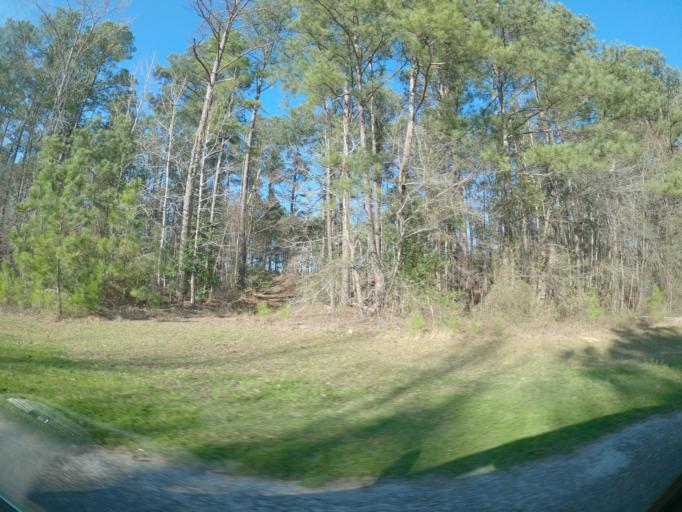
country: US
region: Georgia
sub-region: Columbia County
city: Grovetown
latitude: 33.4553
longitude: -82.2286
